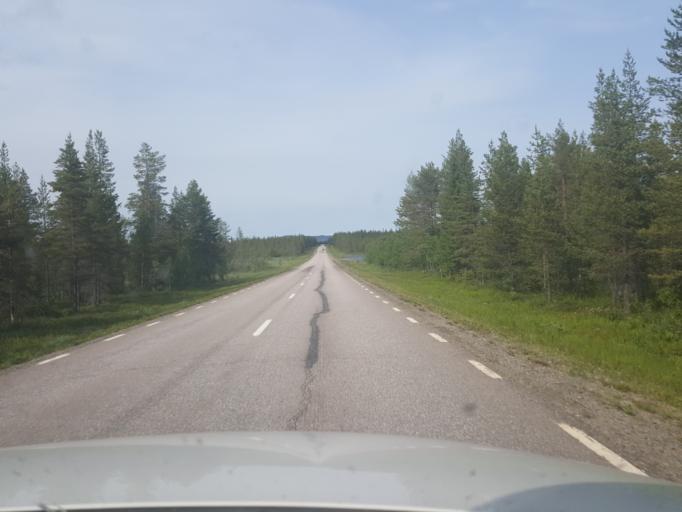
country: SE
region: Norrbotten
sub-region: Arjeplogs Kommun
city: Arjeplog
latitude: 65.7012
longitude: 18.0741
